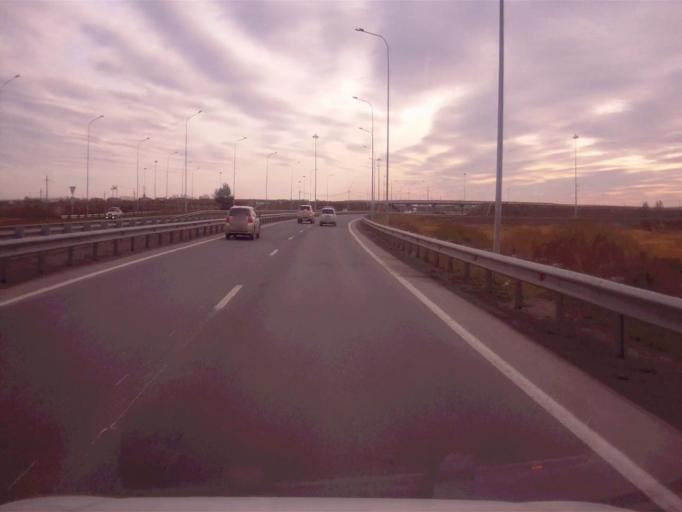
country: RU
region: Chelyabinsk
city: Novosineglazovskiy
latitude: 55.0055
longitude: 61.4537
